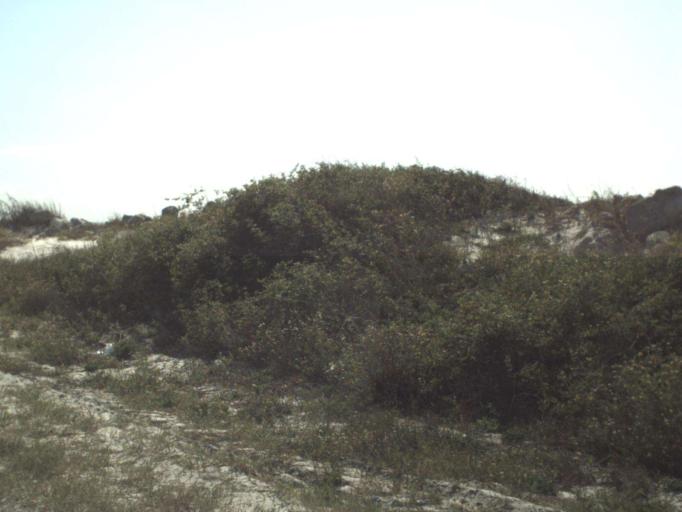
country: US
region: Florida
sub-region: Gulf County
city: Port Saint Joe
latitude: 29.6821
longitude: -85.3666
